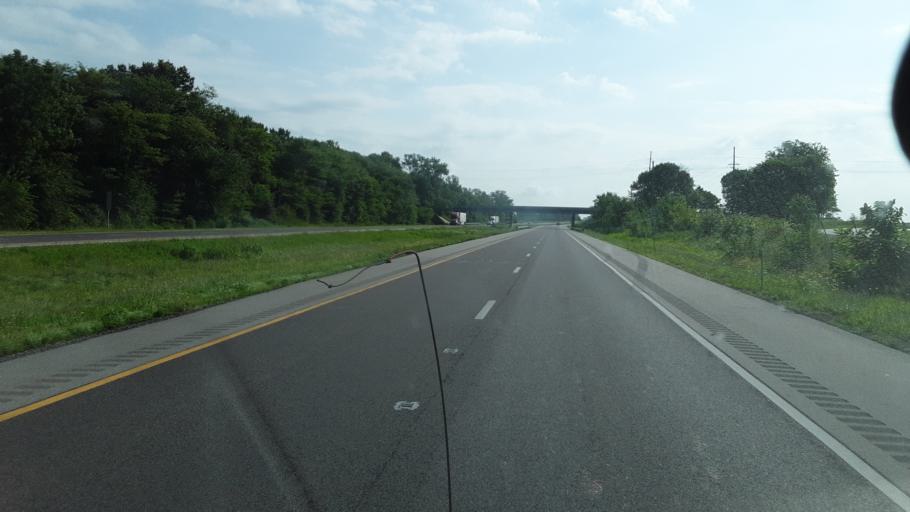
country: US
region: Illinois
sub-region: Madison County
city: Highland
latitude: 38.8003
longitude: -89.6008
